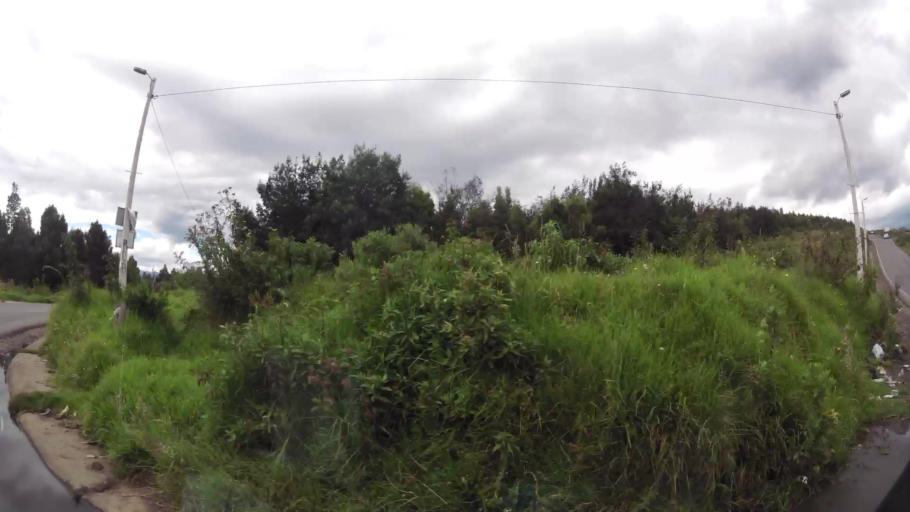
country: EC
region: Pichincha
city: Sangolqui
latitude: -0.3254
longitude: -78.5208
